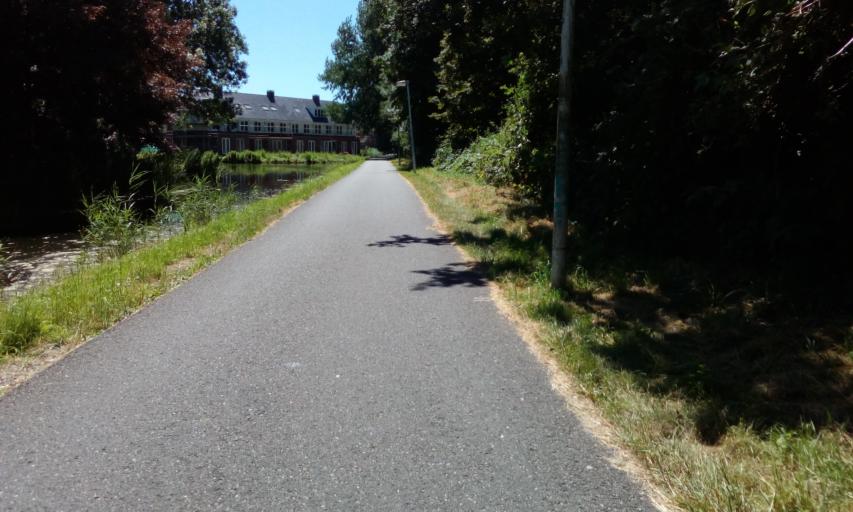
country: NL
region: South Holland
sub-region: Gemeente Teylingen
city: Voorhout
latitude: 52.1973
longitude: 4.4941
